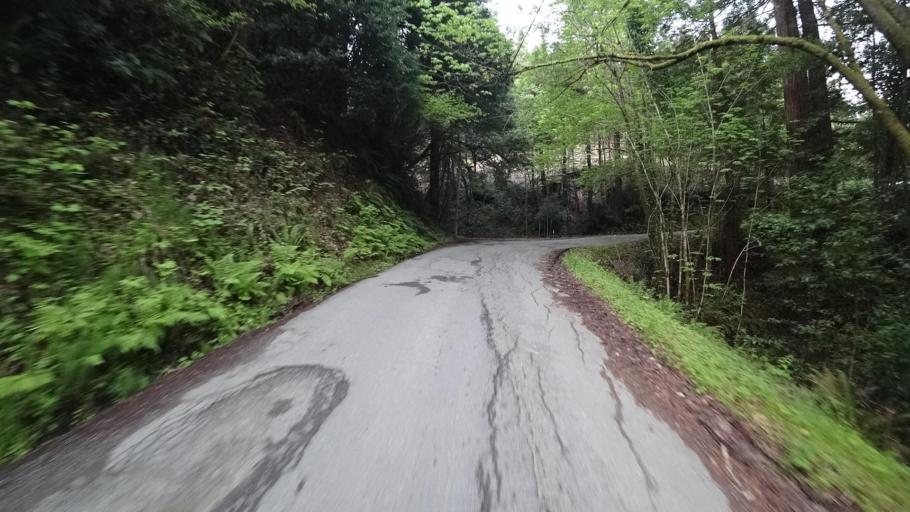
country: US
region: California
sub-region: Humboldt County
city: Redway
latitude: 40.3361
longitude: -123.9076
